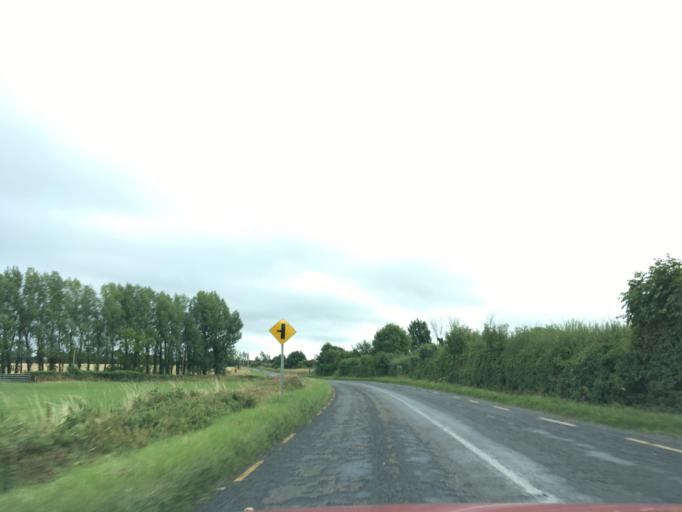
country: IE
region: Munster
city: Cashel
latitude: 52.4493
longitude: -7.8109
